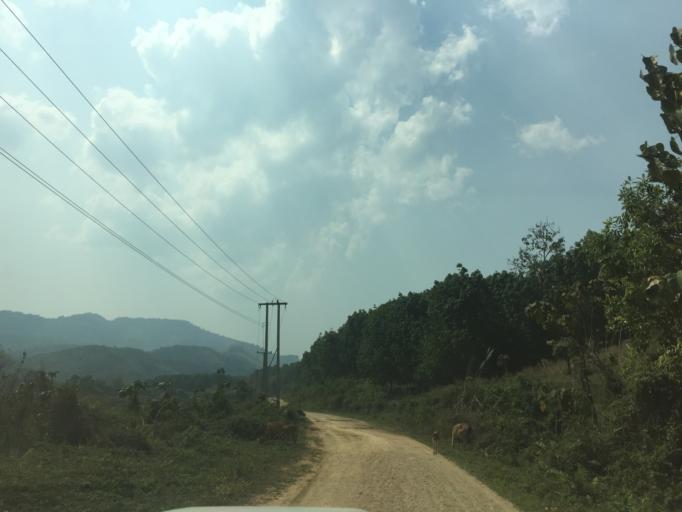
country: TH
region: Nan
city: Thung Chang
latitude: 19.7310
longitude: 100.7400
